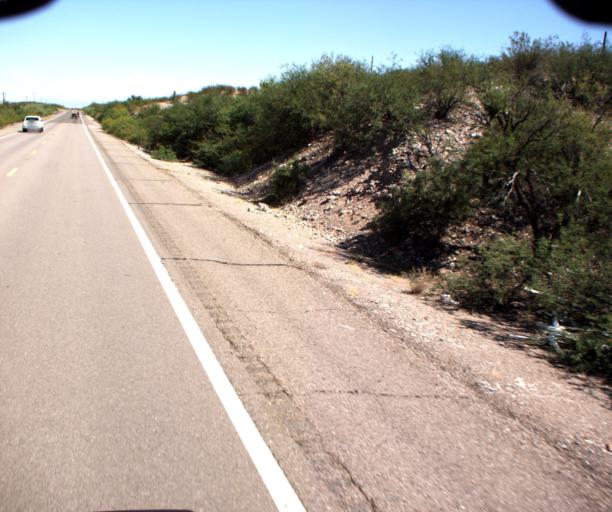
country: US
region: Arizona
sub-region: Pinal County
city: Mammoth
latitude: 32.8016
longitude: -110.6797
